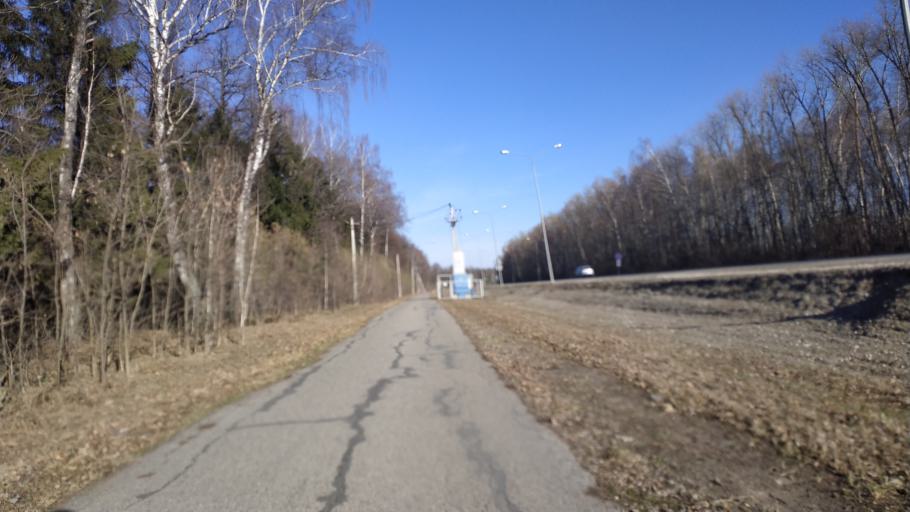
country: RU
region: Chuvashia
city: Ishley
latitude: 56.1340
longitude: 47.1018
